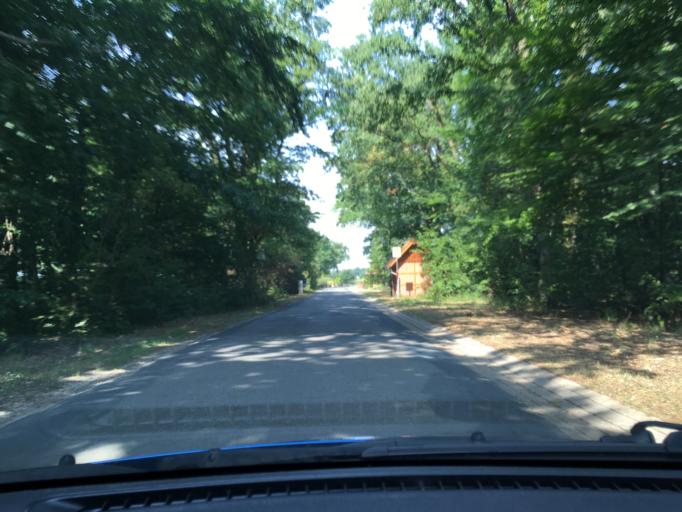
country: DE
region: Lower Saxony
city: Natendorf
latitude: 53.1179
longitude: 10.4349
